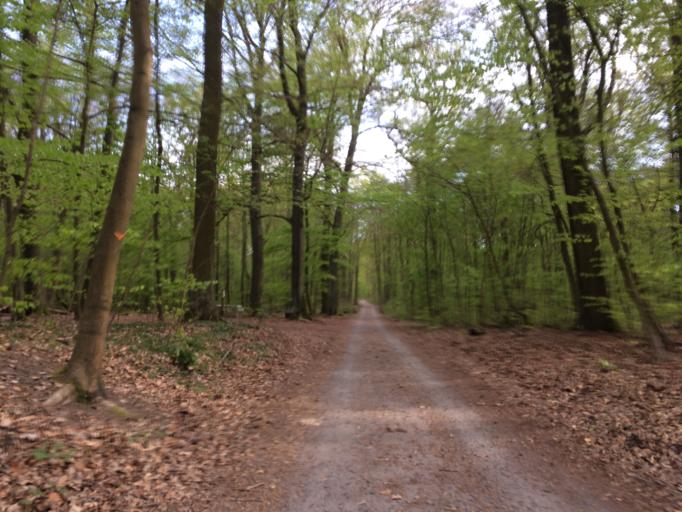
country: DE
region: Berlin
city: Buch
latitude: 52.6467
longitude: 13.4844
